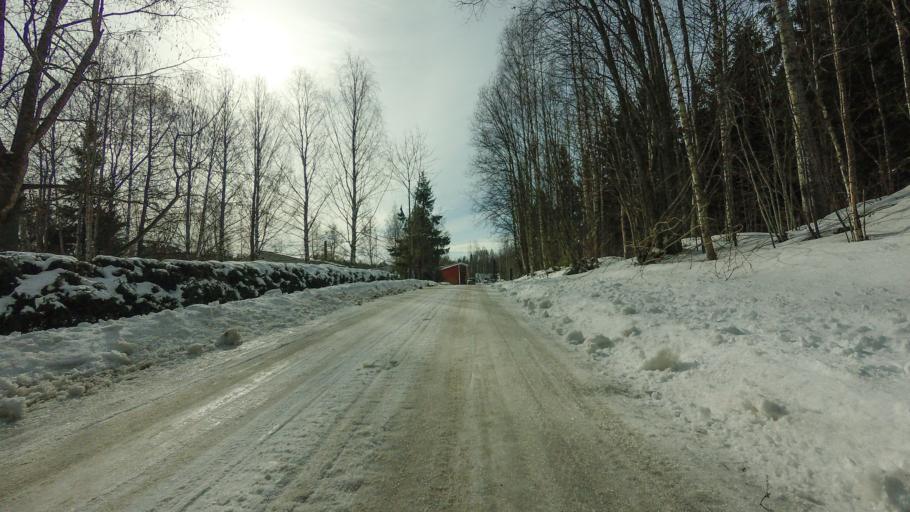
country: FI
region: Southern Savonia
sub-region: Savonlinna
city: Rantasalmi
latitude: 62.1161
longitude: 28.6053
